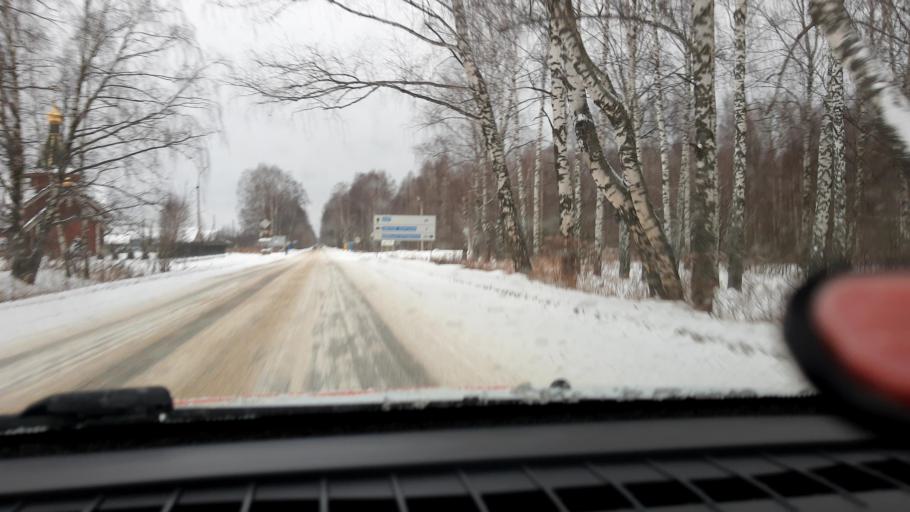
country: RU
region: Nizjnij Novgorod
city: Pamyat' Parizhskoy Kommuny
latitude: 56.2683
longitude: 44.4262
